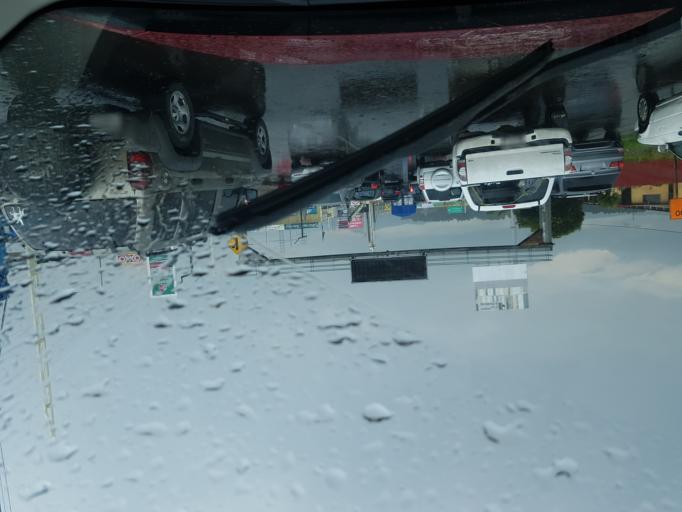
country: MX
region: Mexico
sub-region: Ocoyoacac
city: San Antonio el Llanito
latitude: 19.2814
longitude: -99.4946
